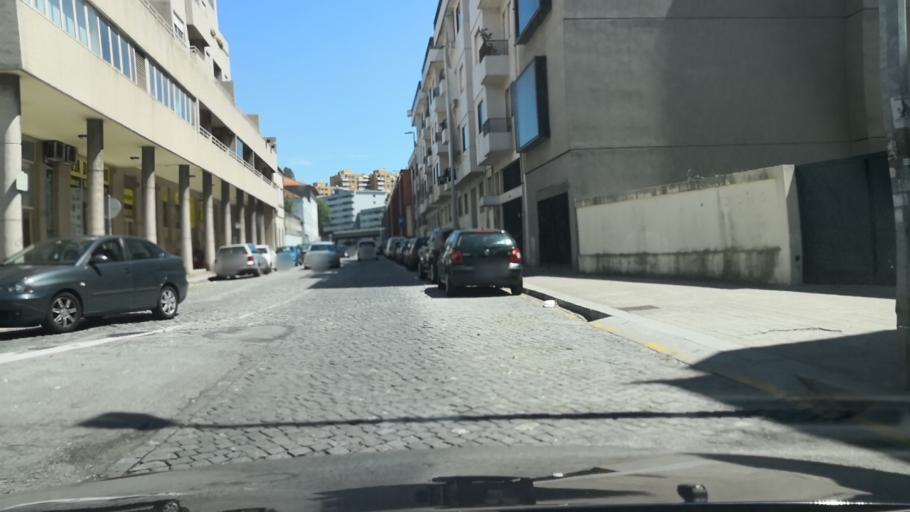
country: PT
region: Porto
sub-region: Vila Nova de Gaia
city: Canidelo
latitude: 41.1548
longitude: -8.6479
